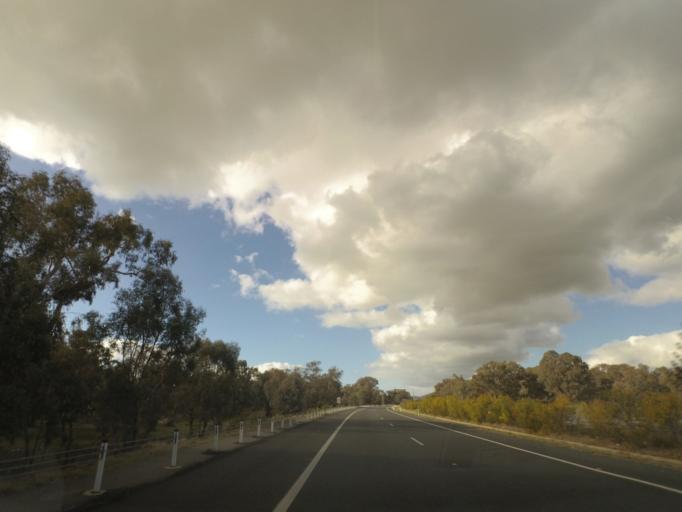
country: AU
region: New South Wales
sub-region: Greater Hume Shire
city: Holbrook
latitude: -35.7065
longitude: 147.3110
